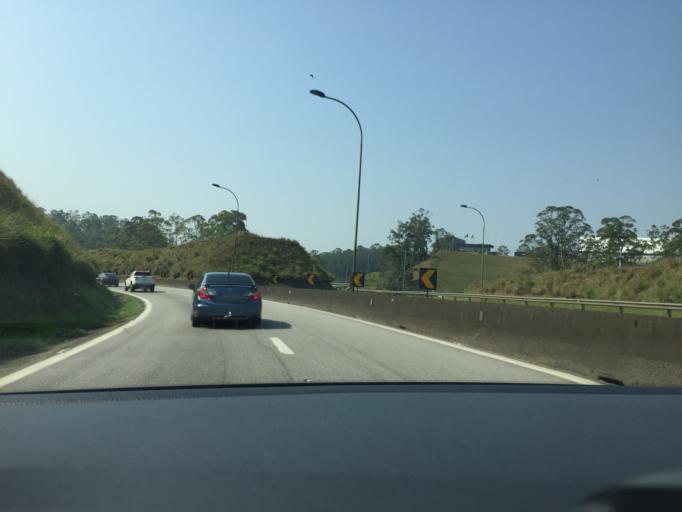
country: BR
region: Sao Paulo
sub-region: Sao Bernardo Do Campo
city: Sao Bernardo do Campo
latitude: -23.7676
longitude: -46.5896
